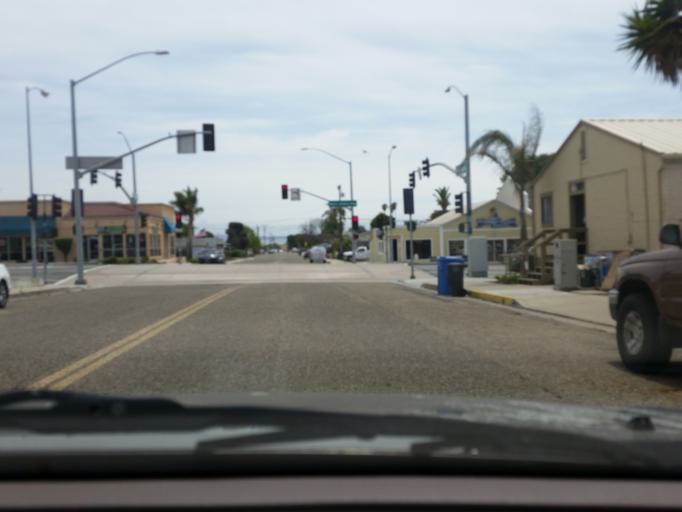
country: US
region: California
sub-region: San Luis Obispo County
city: Grover Beach
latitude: 35.1219
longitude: -120.6190
